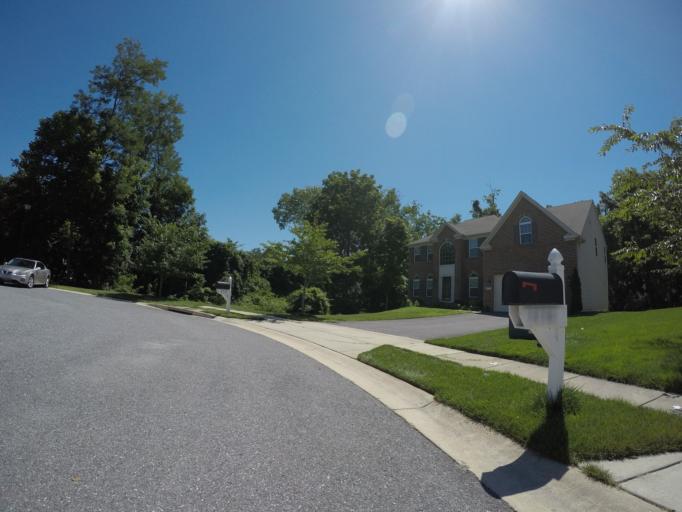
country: US
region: Maryland
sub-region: Howard County
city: Columbia
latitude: 39.2413
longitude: -76.8258
